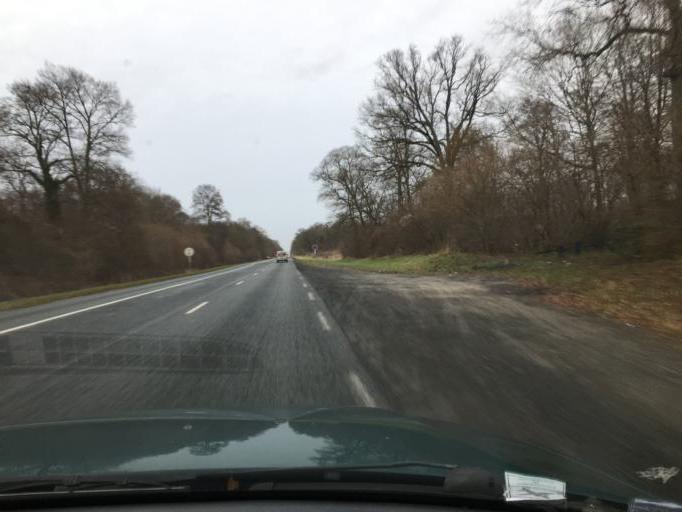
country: FR
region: Picardie
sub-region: Departement de l'Oise
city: Thiers-sur-Theve
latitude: 49.1606
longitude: 2.5530
